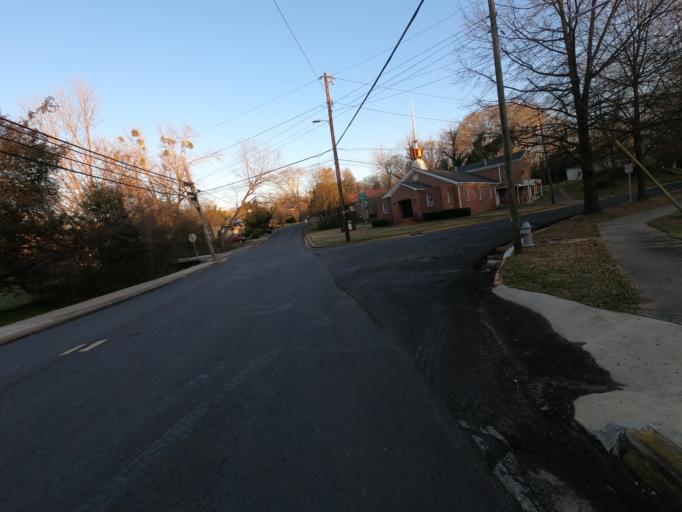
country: US
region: Georgia
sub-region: Clarke County
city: Athens
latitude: 33.9579
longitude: -83.3642
